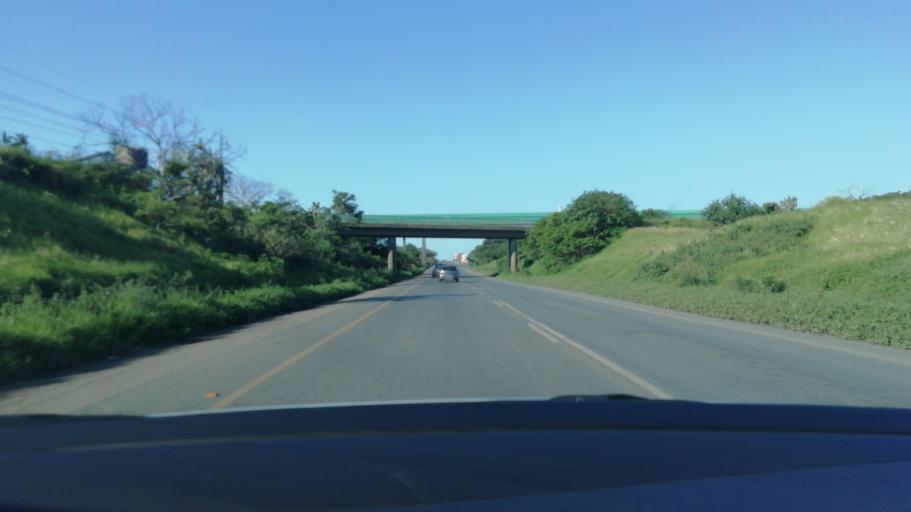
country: ZA
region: KwaZulu-Natal
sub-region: uThungulu District Municipality
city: Richards Bay
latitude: -28.7796
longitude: 32.0292
